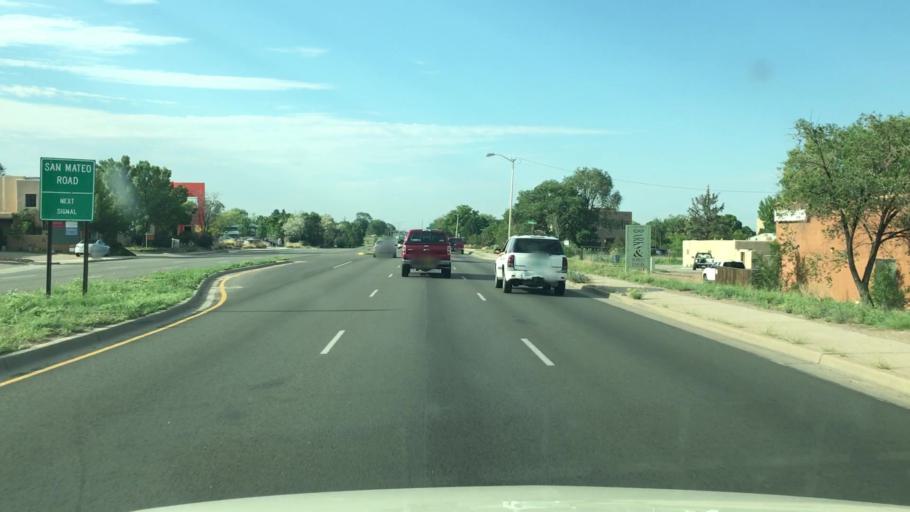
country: US
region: New Mexico
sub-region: Santa Fe County
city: Santa Fe
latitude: 35.6677
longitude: -105.9562
